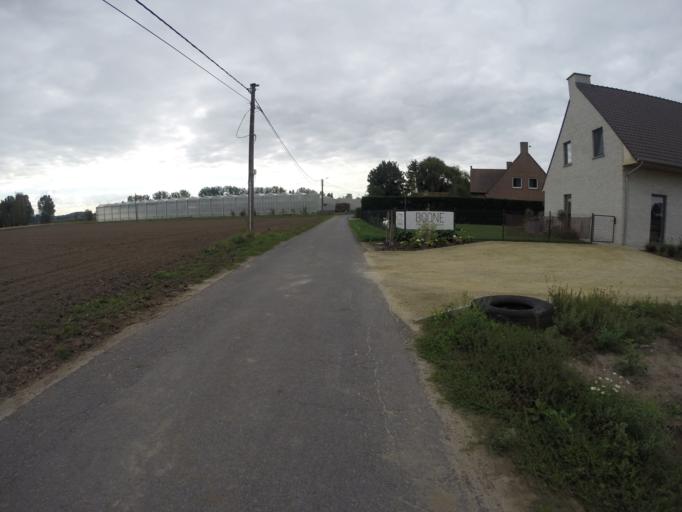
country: BE
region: Flanders
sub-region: Provincie West-Vlaanderen
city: Ruiselede
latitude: 51.0527
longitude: 3.4200
